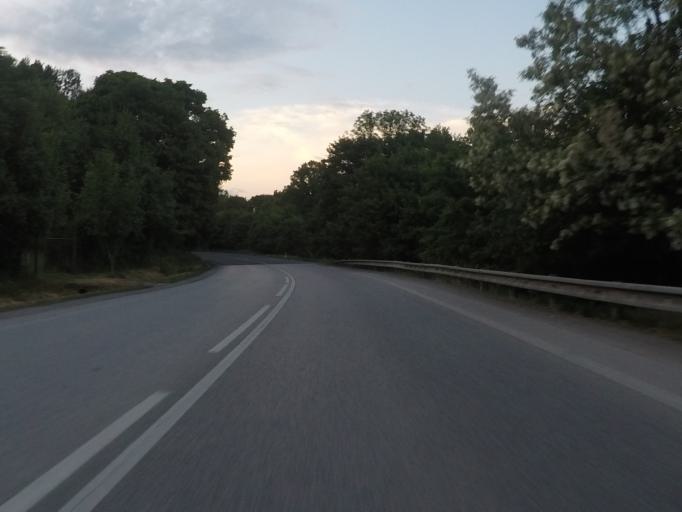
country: SK
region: Banskobystricky
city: Rimavska Sobota
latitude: 48.4735
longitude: 19.9501
